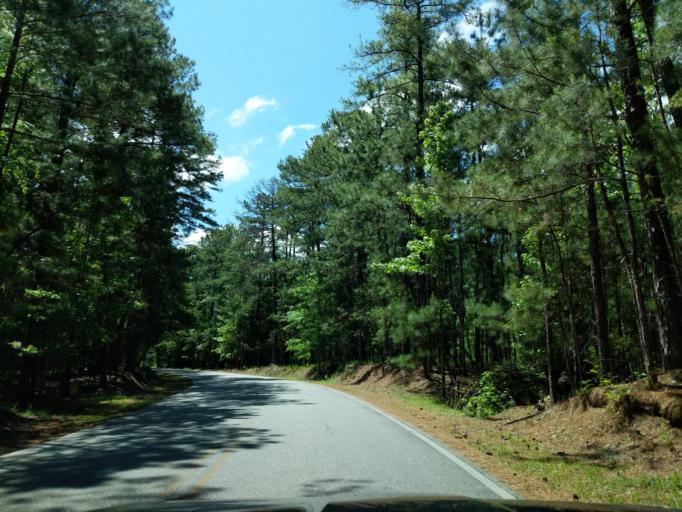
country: US
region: Georgia
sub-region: Columbia County
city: Appling
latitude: 33.6503
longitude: -82.3902
